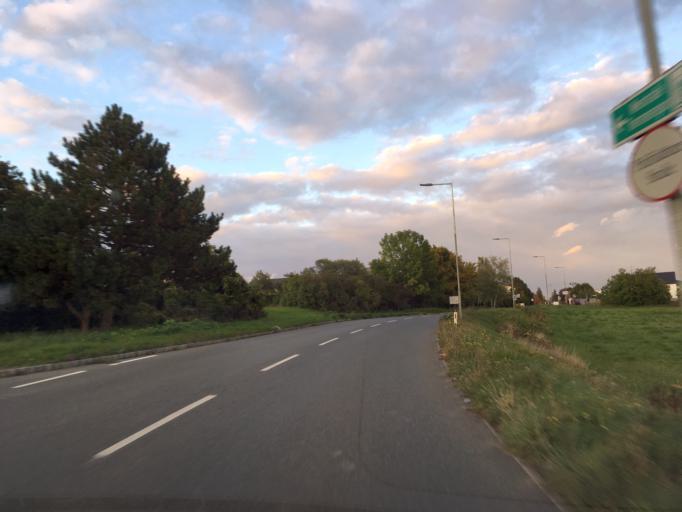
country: AT
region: Lower Austria
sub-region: Politischer Bezirk Baden
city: Pfaffstatten
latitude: 48.0151
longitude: 16.2530
